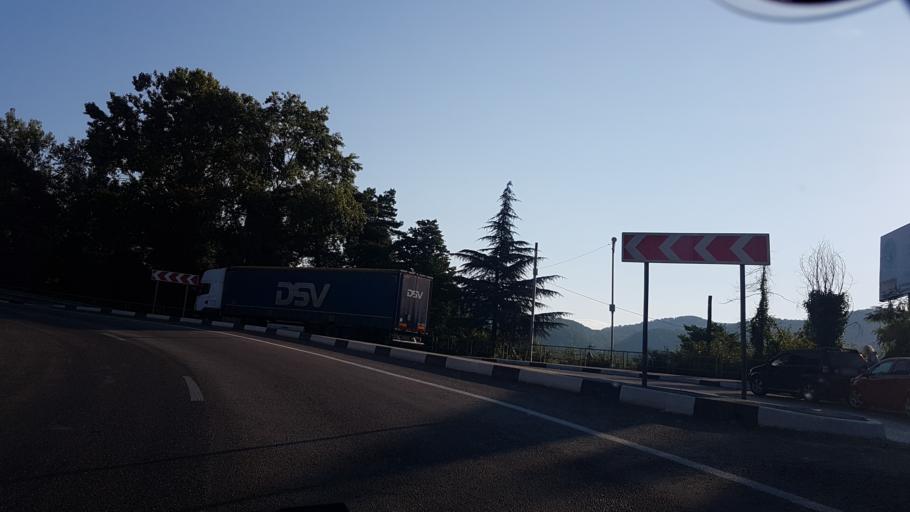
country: RU
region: Krasnodarskiy
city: Dagomys
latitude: 43.6432
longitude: 39.7017
